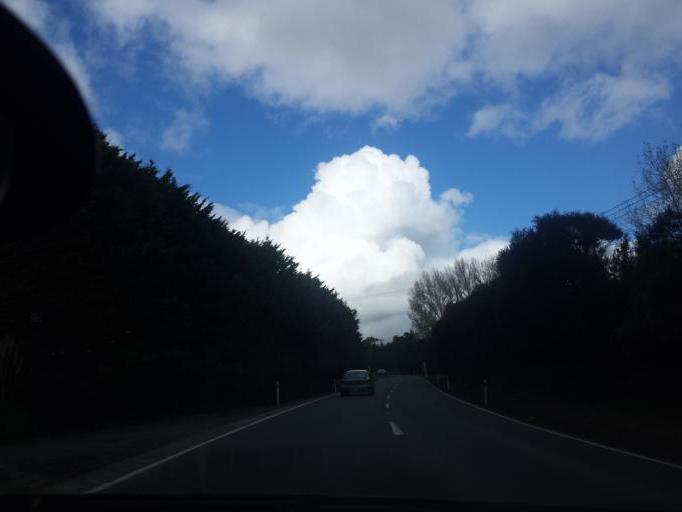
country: NZ
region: Auckland
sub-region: Auckland
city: Warkworth
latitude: -36.3963
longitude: 174.6755
